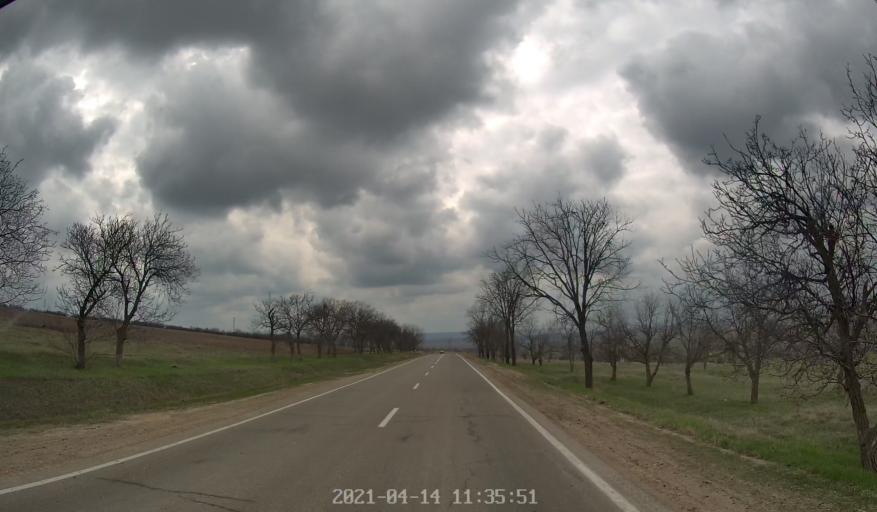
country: MD
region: Criuleni
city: Criuleni
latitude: 47.1655
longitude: 29.1633
